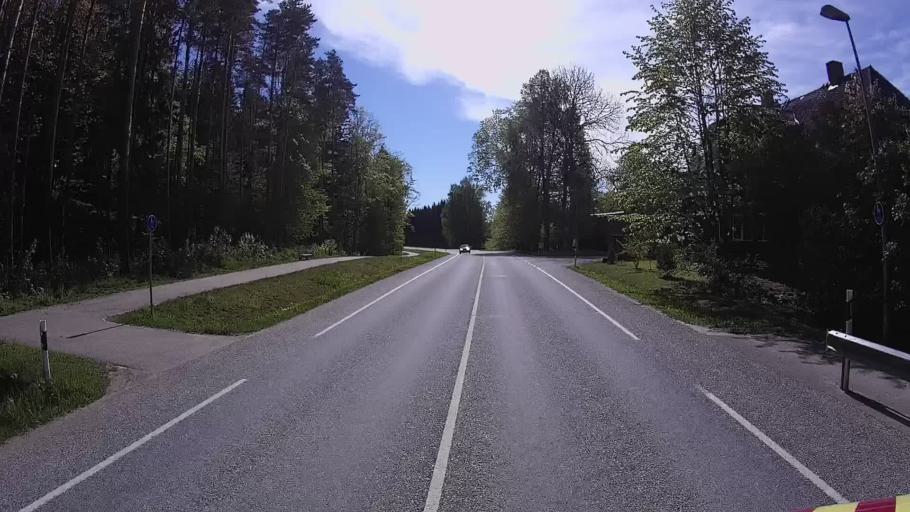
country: EE
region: Polvamaa
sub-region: Raepina vald
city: Rapina
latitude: 58.0842
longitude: 27.4949
